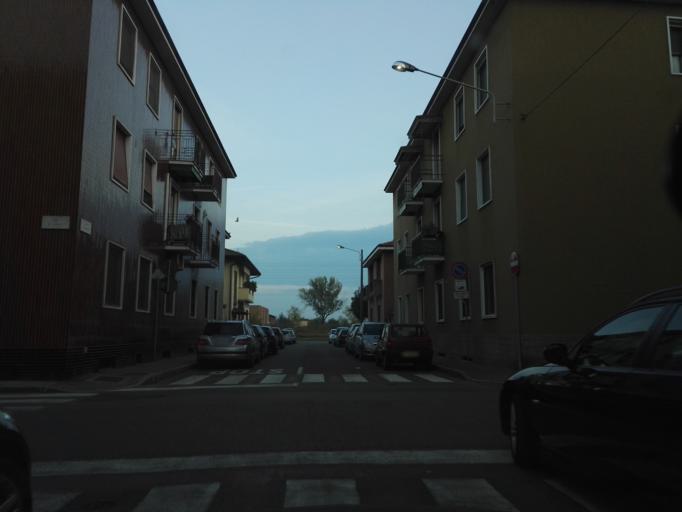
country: IT
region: Lombardy
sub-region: Citta metropolitana di Milano
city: San Giuliano Milanese
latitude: 45.3922
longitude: 9.2891
